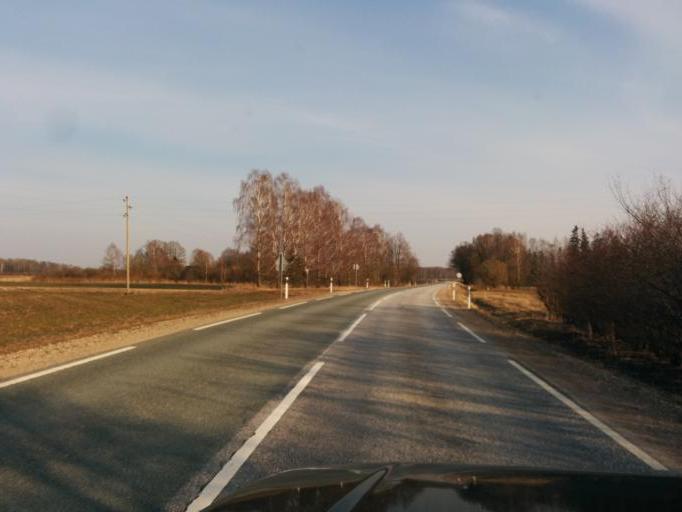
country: LV
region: Lecava
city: Iecava
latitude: 56.5937
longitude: 24.1291
